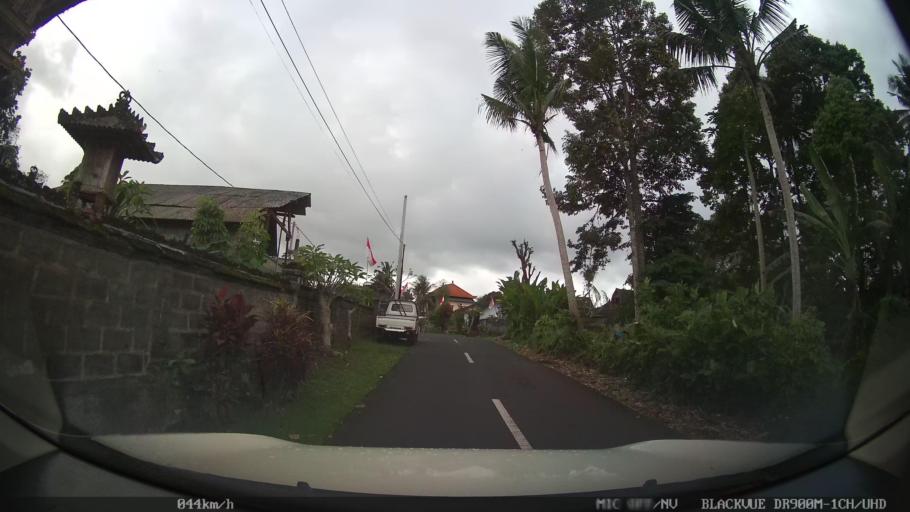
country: ID
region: Bali
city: Banjar Cemenggon
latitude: -8.5348
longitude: 115.1923
